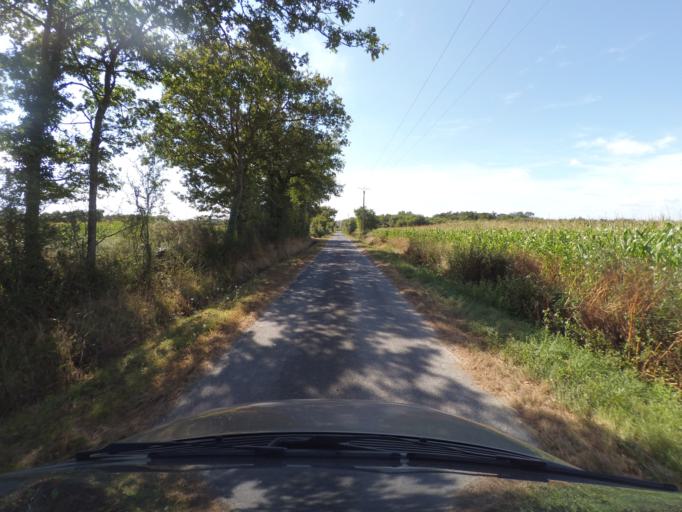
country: FR
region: Pays de la Loire
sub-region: Departement de la Loire-Atlantique
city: Le Bignon
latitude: 47.0902
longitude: -1.4673
